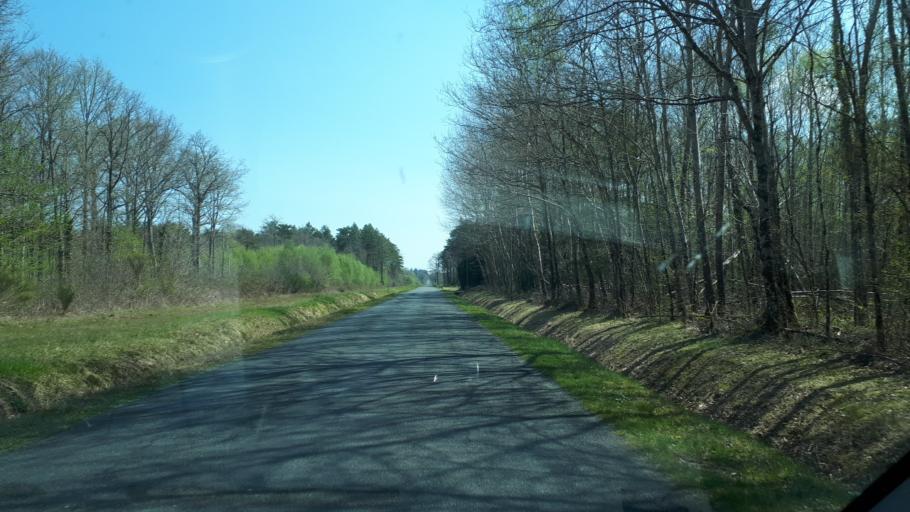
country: FR
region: Centre
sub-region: Departement du Cher
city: Neuvy-sur-Barangeon
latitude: 47.3178
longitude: 2.1481
